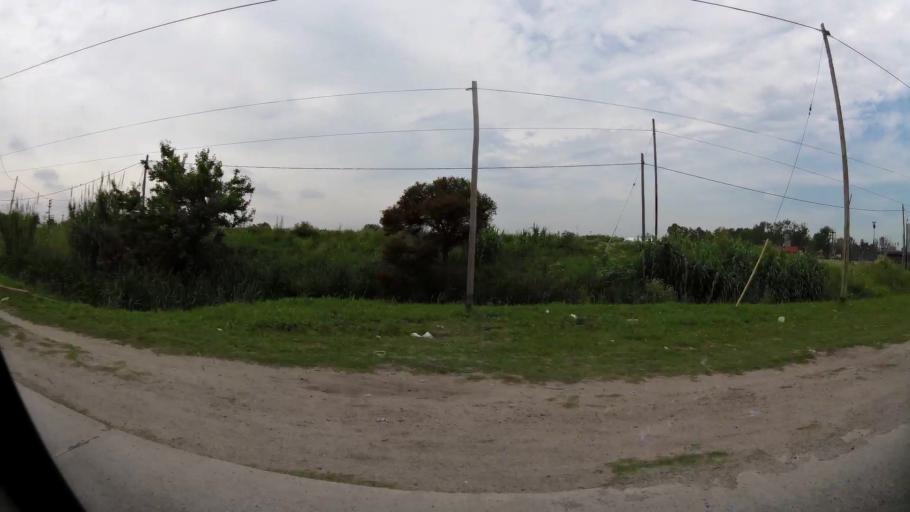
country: AR
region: Buenos Aires
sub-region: Partido de La Plata
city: La Plata
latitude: -34.9023
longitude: -57.9955
